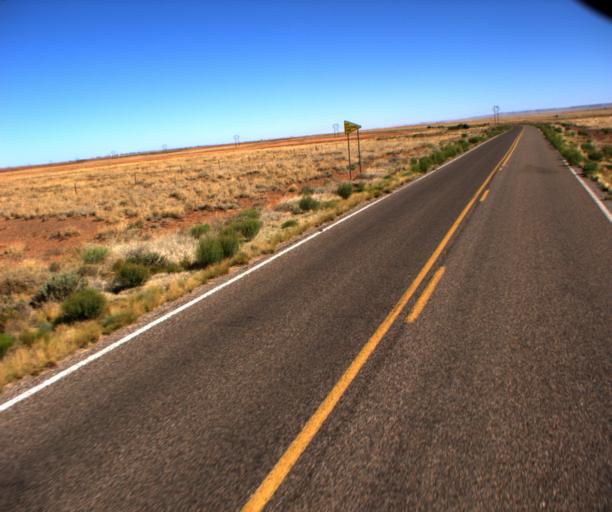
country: US
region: Arizona
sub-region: Coconino County
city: LeChee
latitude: 35.2487
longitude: -110.9612
